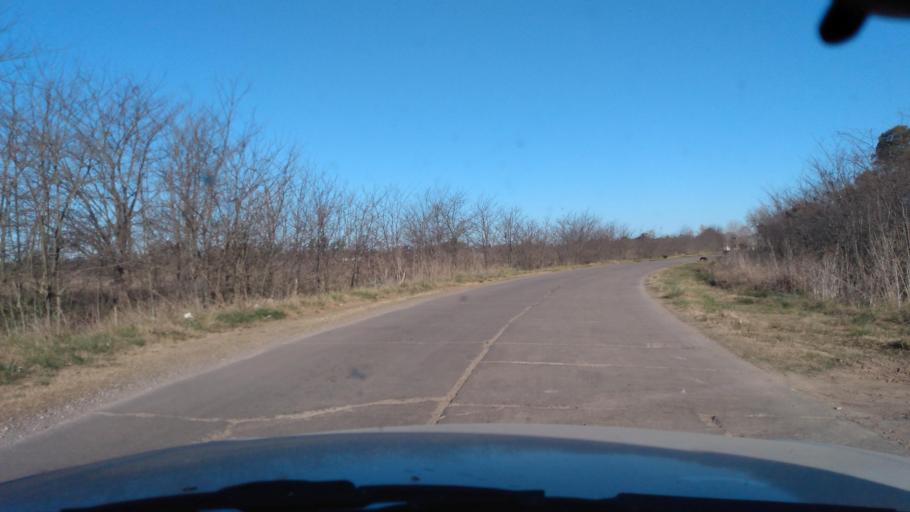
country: AR
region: Buenos Aires
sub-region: Partido de Lujan
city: Lujan
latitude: -34.6181
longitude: -59.2588
